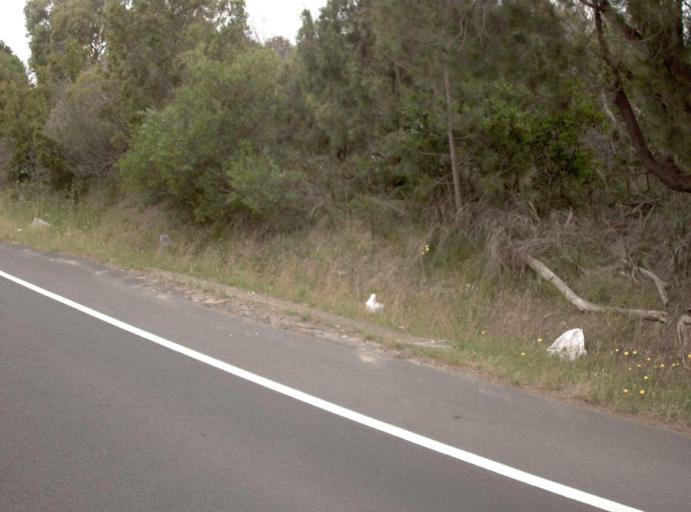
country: AU
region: Victoria
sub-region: Mornington Peninsula
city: Mount Martha
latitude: -38.2798
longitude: 145.0329
